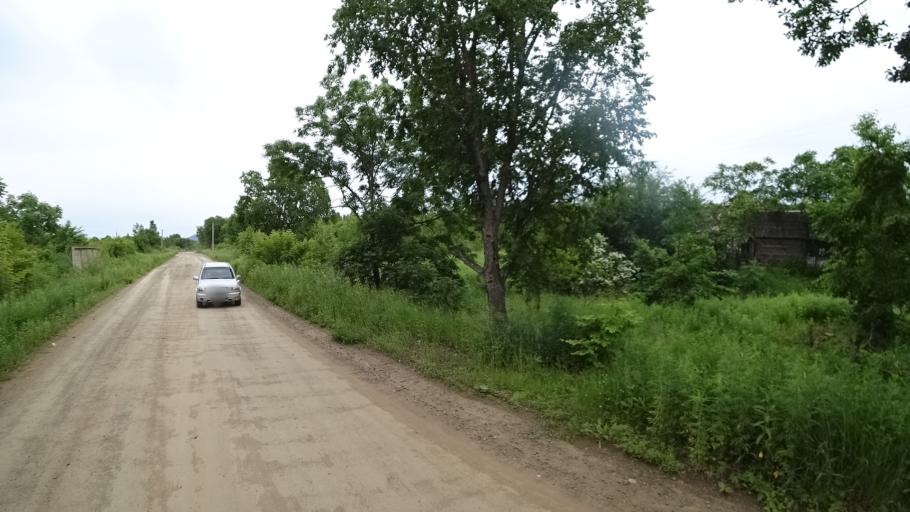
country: RU
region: Primorskiy
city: Arsen'yev
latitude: 44.1962
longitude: 133.3081
